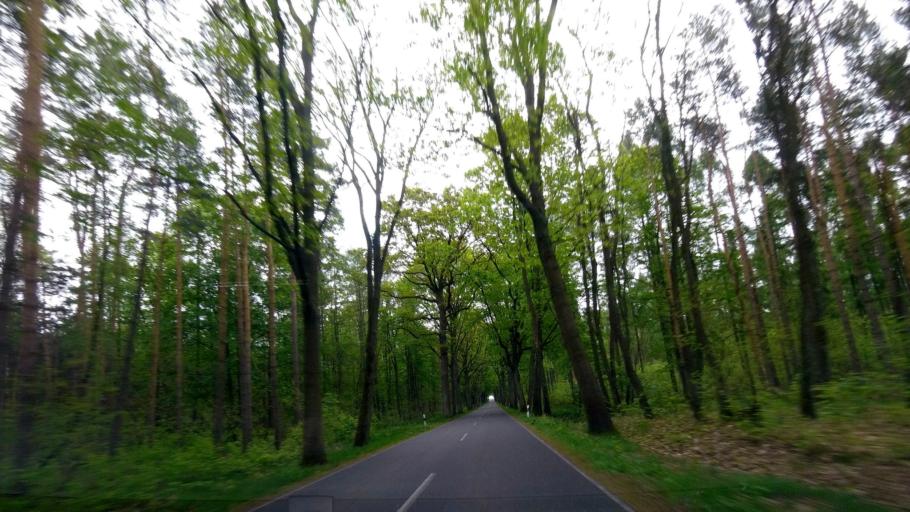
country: DE
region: Brandenburg
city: Ihlow
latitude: 51.9205
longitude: 13.3832
